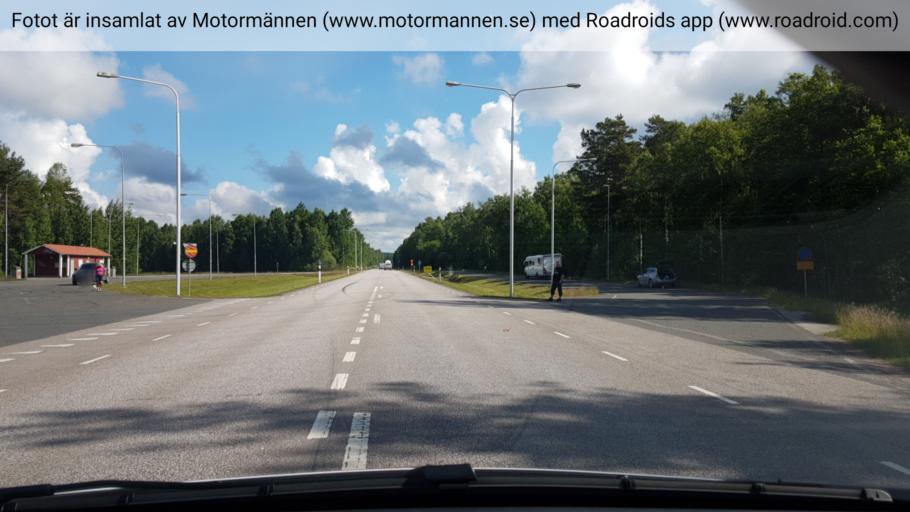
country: SE
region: Vaestra Goetaland
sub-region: Karlsborgs Kommun
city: Karlsborg
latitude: 58.5762
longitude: 14.4964
